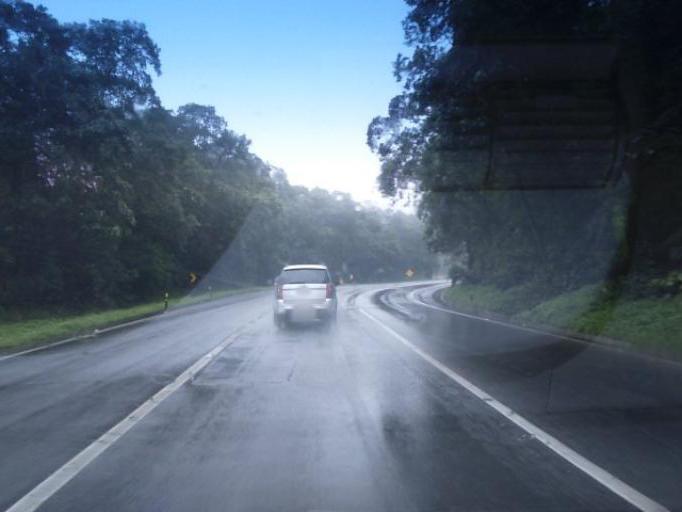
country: BR
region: Parana
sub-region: Guaratuba
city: Guaratuba
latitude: -25.8563
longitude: -48.9500
